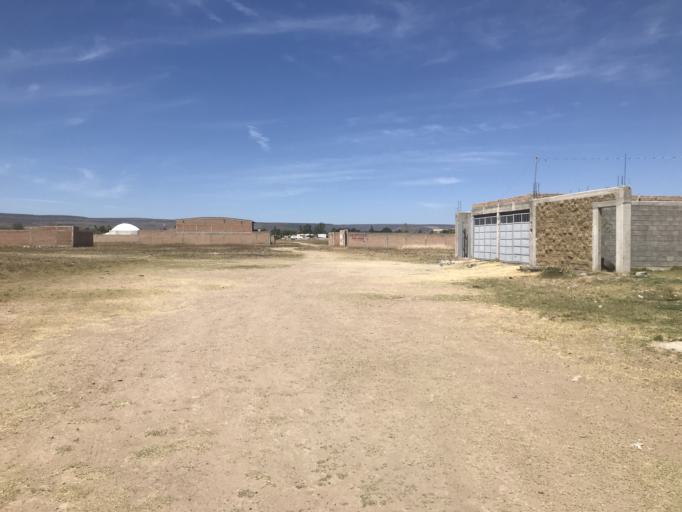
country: MX
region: Durango
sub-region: Durango
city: Sebastian Lerdo de Tejada
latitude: 23.9772
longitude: -104.6534
